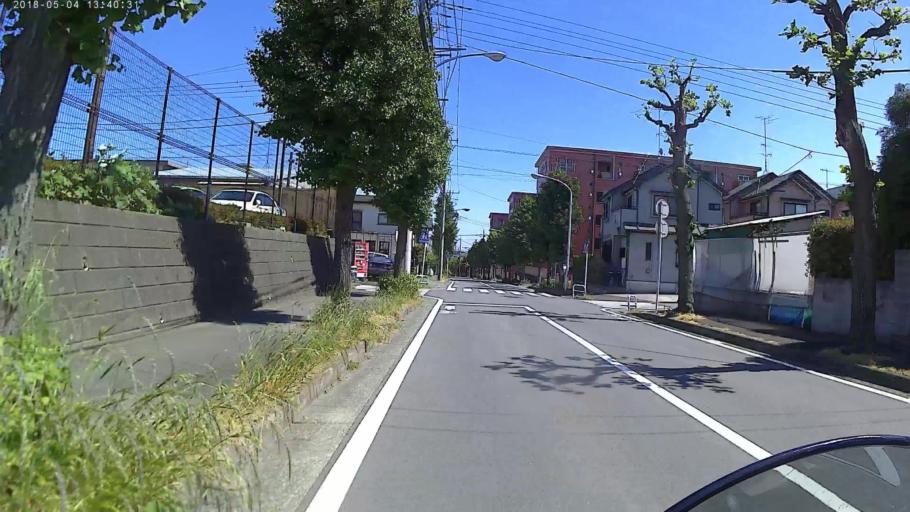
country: JP
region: Kanagawa
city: Minami-rinkan
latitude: 35.4425
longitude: 139.4551
